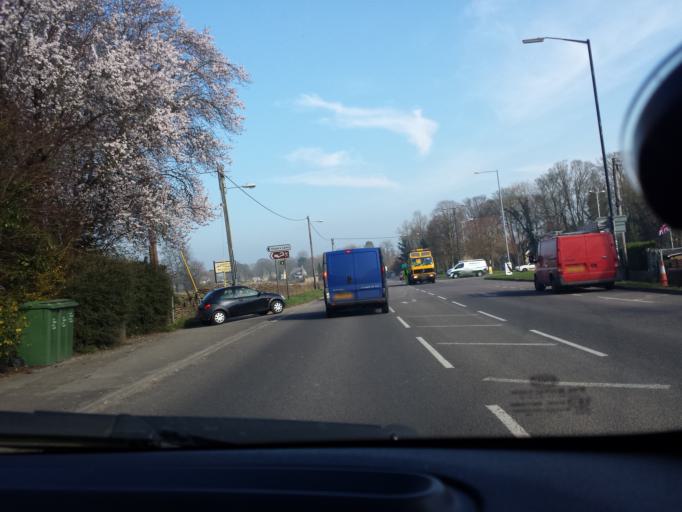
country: GB
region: England
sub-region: Wiltshire
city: Neston
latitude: 51.4329
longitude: -2.2086
